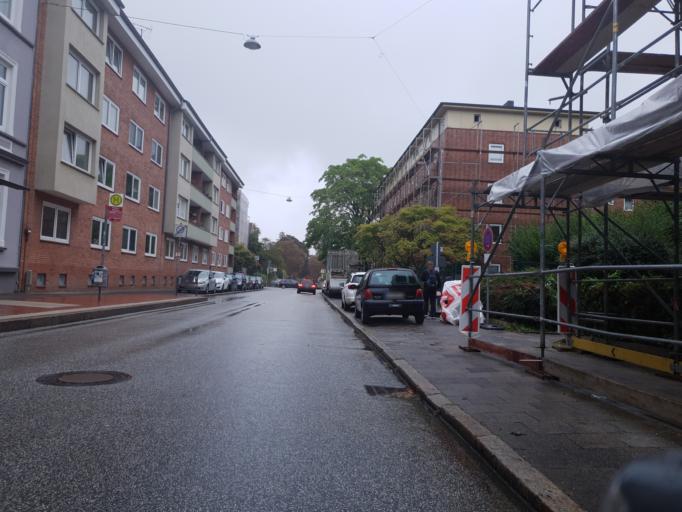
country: DE
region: Schleswig-Holstein
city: Kiel
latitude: 54.3353
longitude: 10.1388
